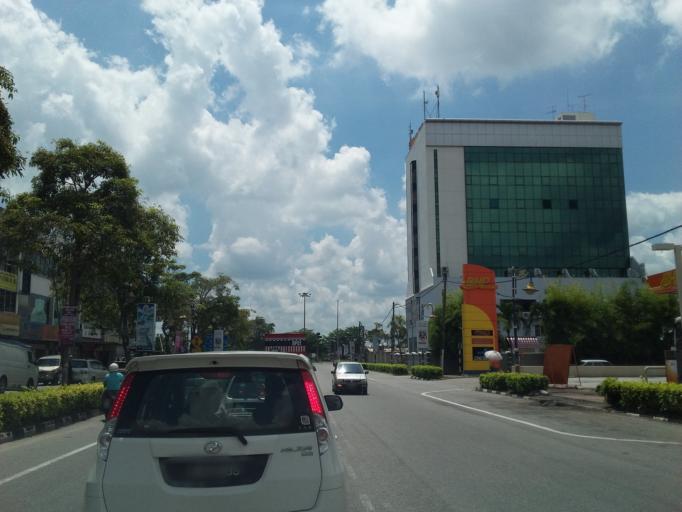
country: MY
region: Johor
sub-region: Daerah Batu Pahat
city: Batu Pahat
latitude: 1.8579
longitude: 102.9268
